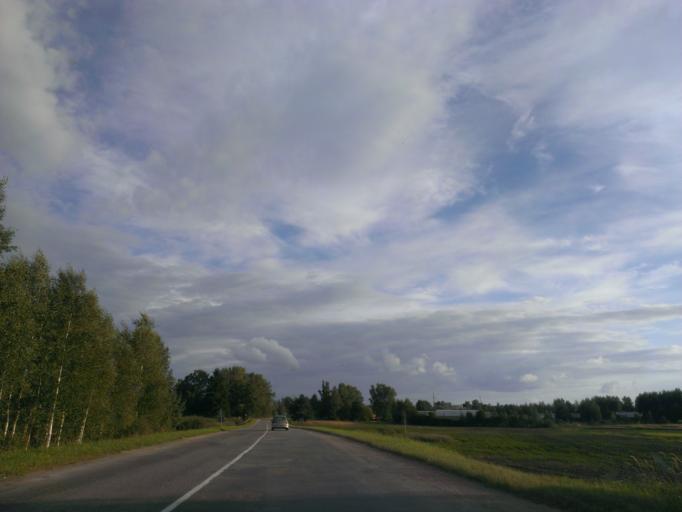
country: LV
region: Ikskile
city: Ikskile
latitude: 56.8504
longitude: 24.5034
